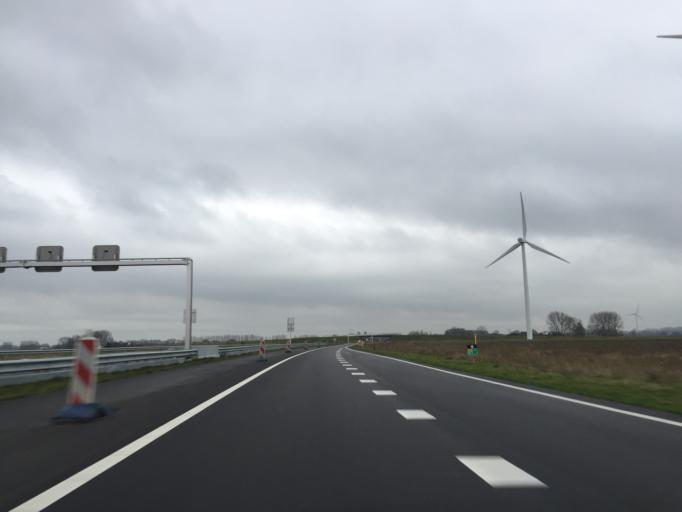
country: NL
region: Zeeland
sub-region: Gemeente Terneuzen
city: Sluiskil
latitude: 51.2908
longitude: 3.8679
